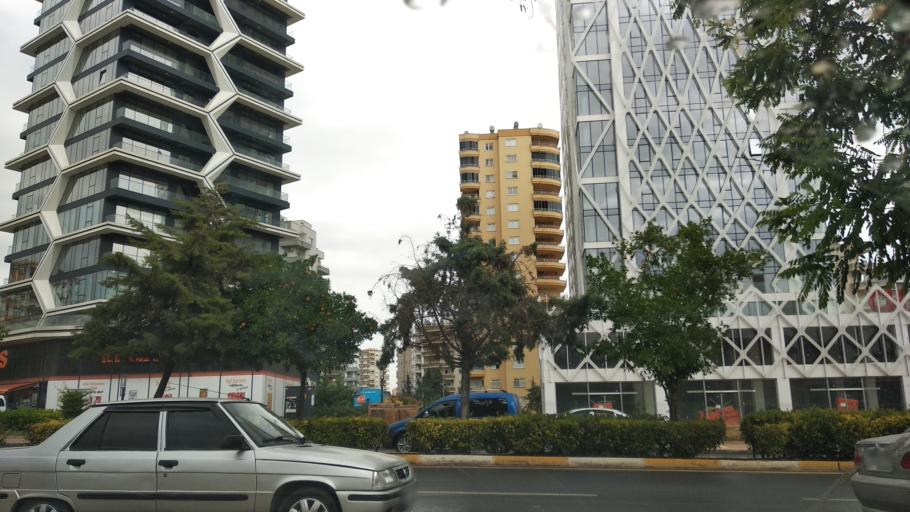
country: TR
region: Mersin
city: Mercin
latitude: 36.7877
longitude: 34.5880
